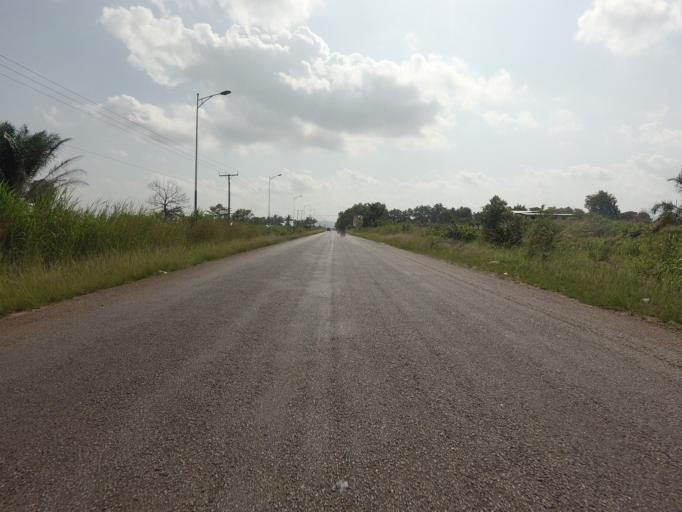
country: GH
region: Volta
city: Ho
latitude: 6.5972
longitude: 0.5215
